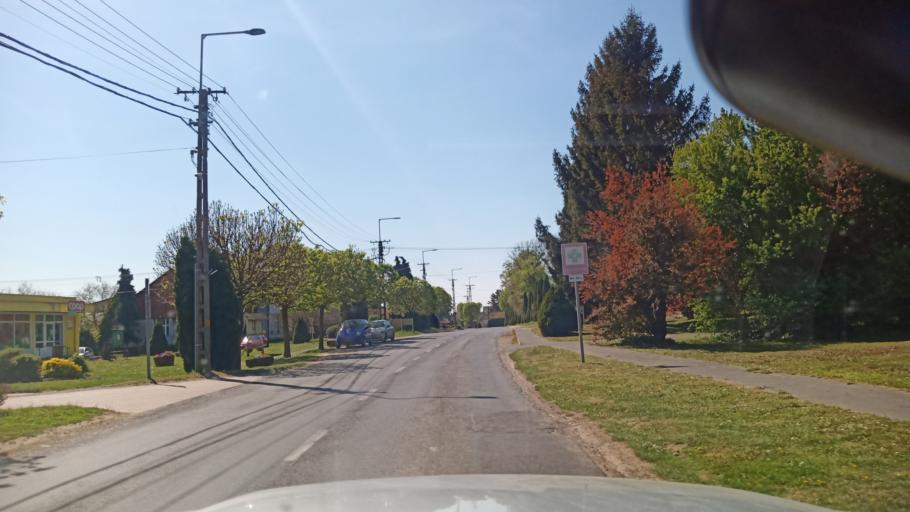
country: HU
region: Zala
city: Sarmellek
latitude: 46.7392
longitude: 17.1066
